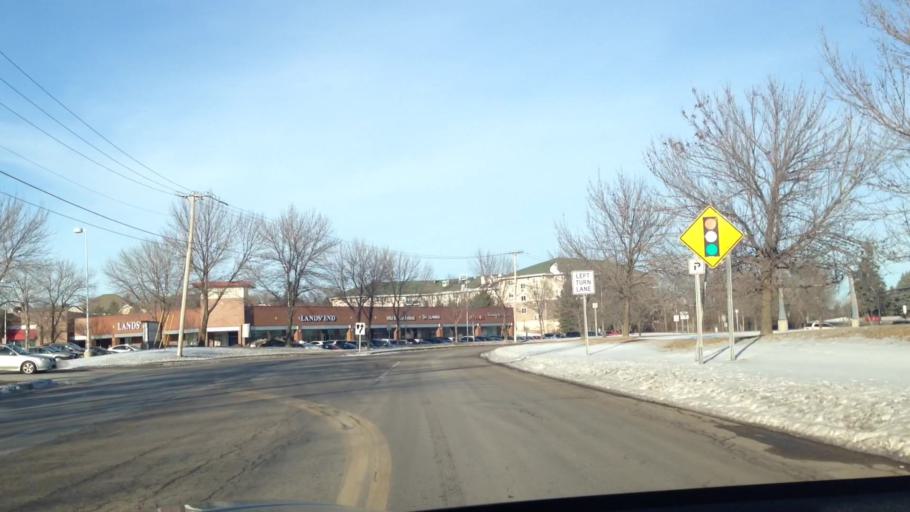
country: US
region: Minnesota
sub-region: Hennepin County
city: Minnetonka Mills
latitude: 44.9720
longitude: -93.4220
